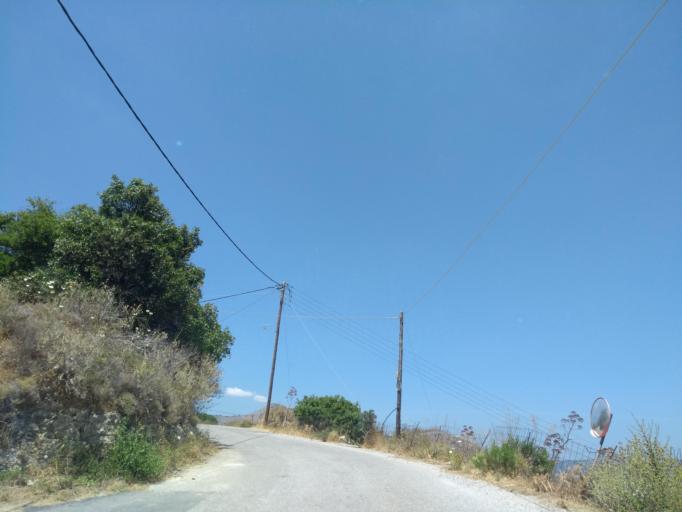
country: GR
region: Crete
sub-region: Nomos Chanias
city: Georgioupolis
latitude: 35.3157
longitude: 24.2911
